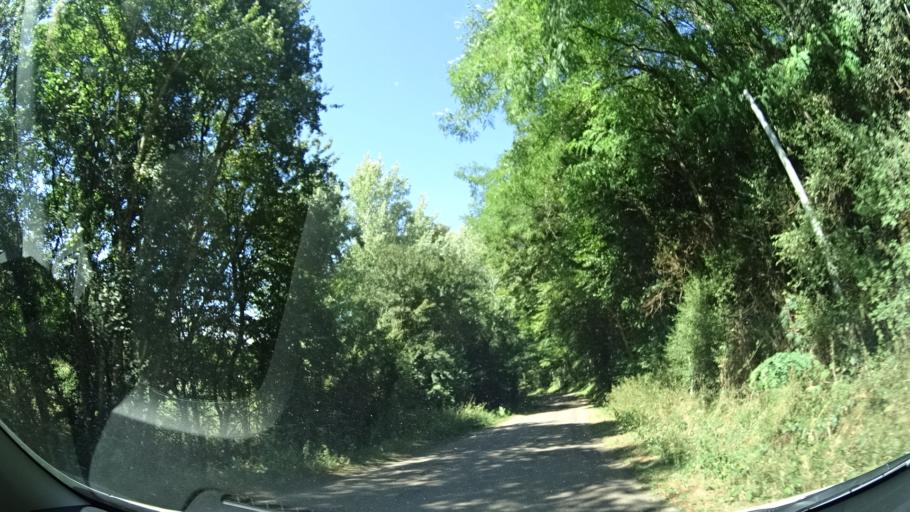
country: FR
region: Centre
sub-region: Departement du Loiret
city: Trigueres
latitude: 47.9444
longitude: 2.9851
